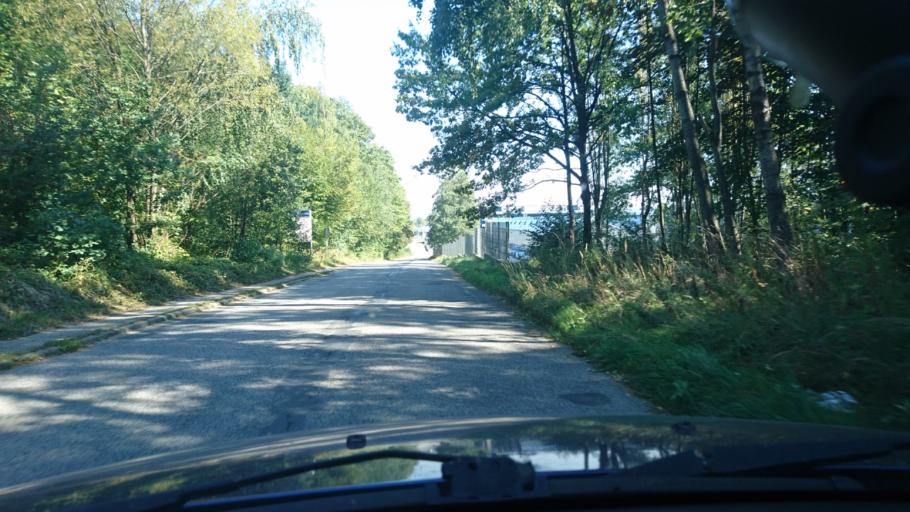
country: PL
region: Silesian Voivodeship
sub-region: Bielsko-Biala
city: Bielsko-Biala
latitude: 49.8414
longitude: 19.0300
